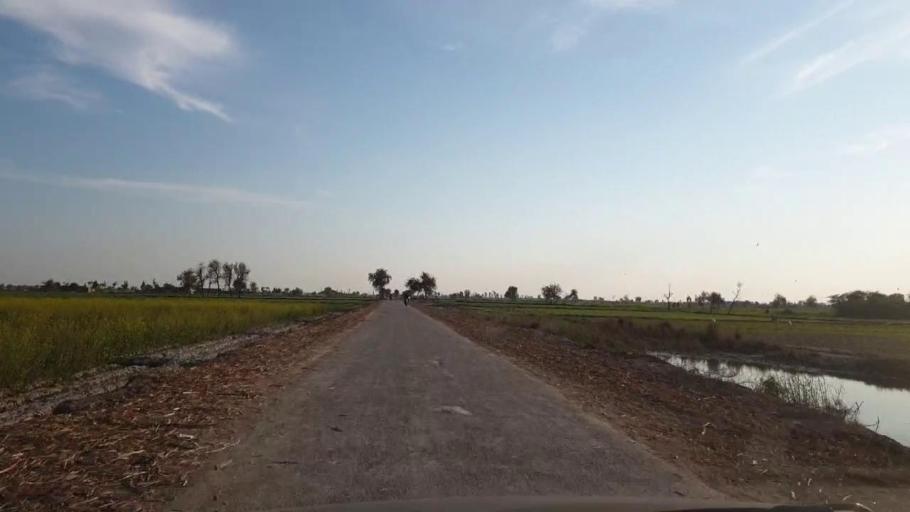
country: PK
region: Sindh
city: Khadro
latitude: 26.1686
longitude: 68.7531
